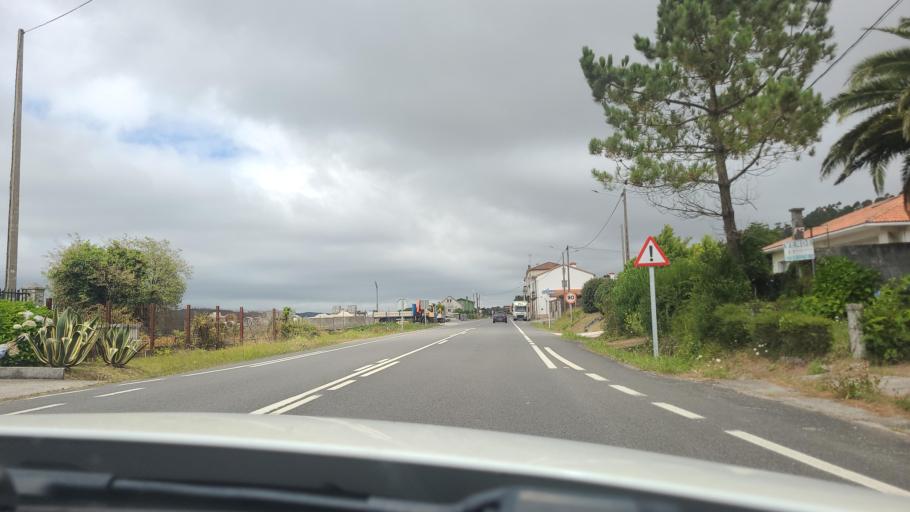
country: ES
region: Galicia
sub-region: Provincia da Coruna
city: Cee
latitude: 42.9879
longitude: -9.1844
